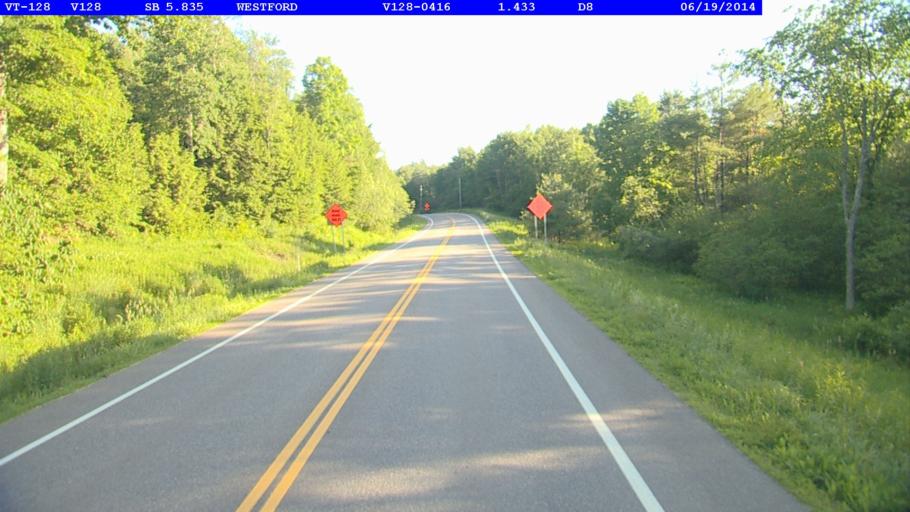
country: US
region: Vermont
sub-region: Chittenden County
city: Jericho
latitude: 44.5786
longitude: -73.0192
